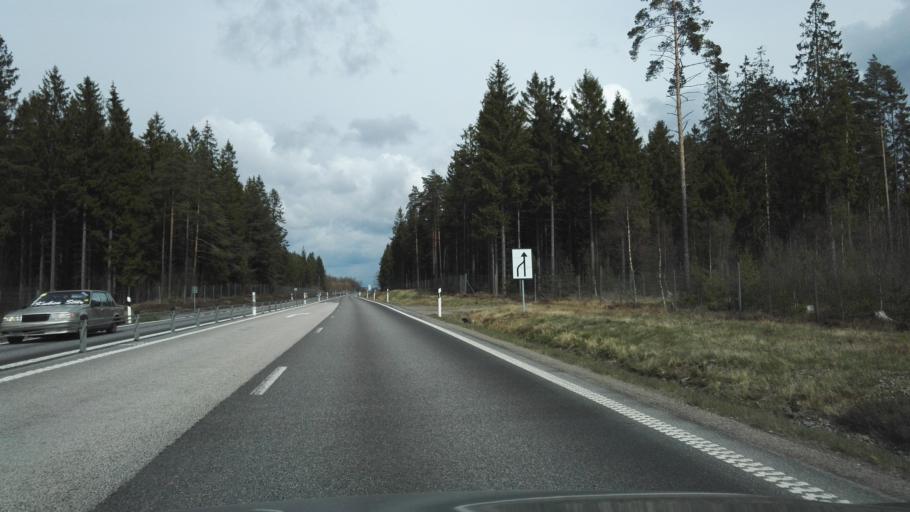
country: SE
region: Kronoberg
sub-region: Vaxjo Kommun
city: Rottne
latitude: 56.9565
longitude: 14.9401
